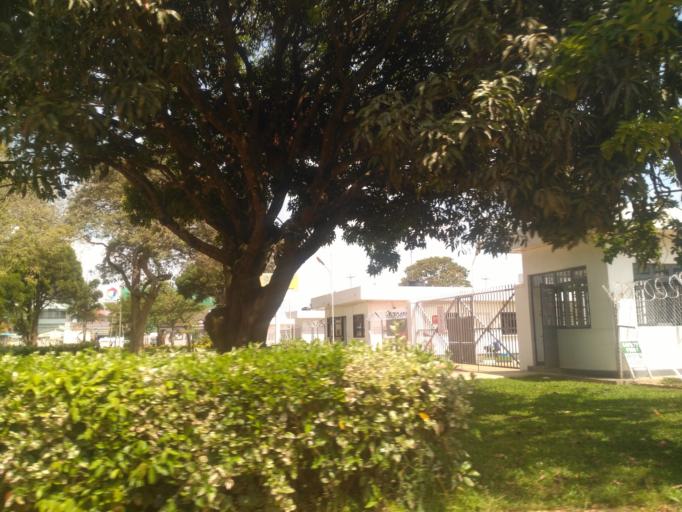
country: UG
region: Central Region
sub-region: Wakiso District
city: Entebbe
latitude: 0.0423
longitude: 32.4435
